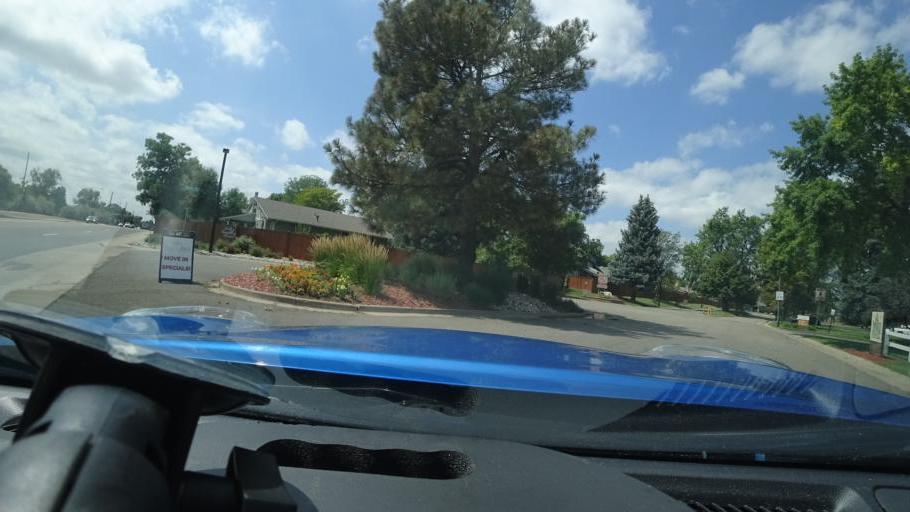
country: US
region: Colorado
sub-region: Adams County
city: Aurora
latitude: 39.7135
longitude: -104.8474
